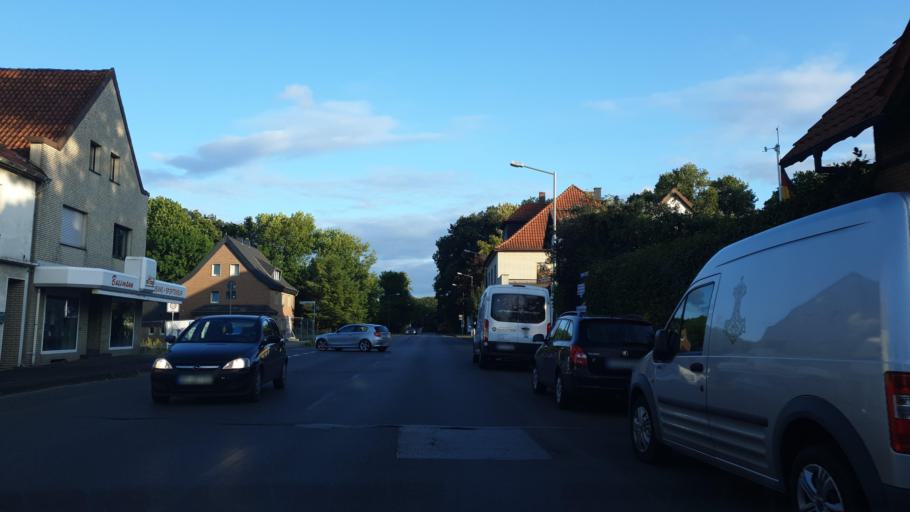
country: DE
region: North Rhine-Westphalia
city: Loehne
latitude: 52.2157
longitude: 8.7120
